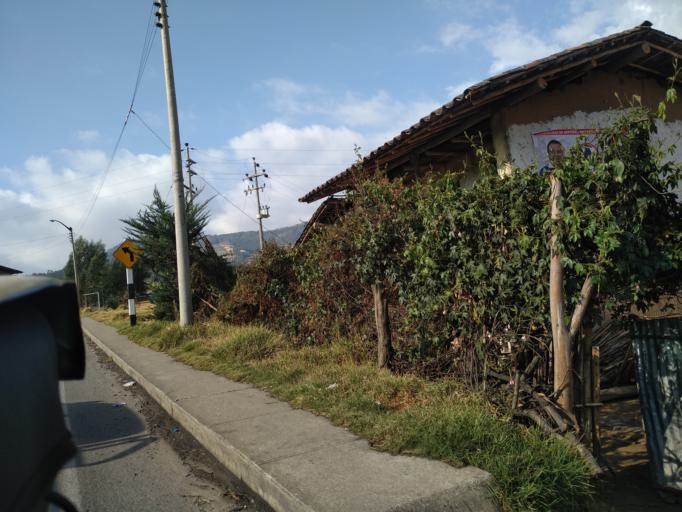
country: PE
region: La Libertad
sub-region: Provincia de Otuzco
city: Agallpampa
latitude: -7.9954
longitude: -78.5204
